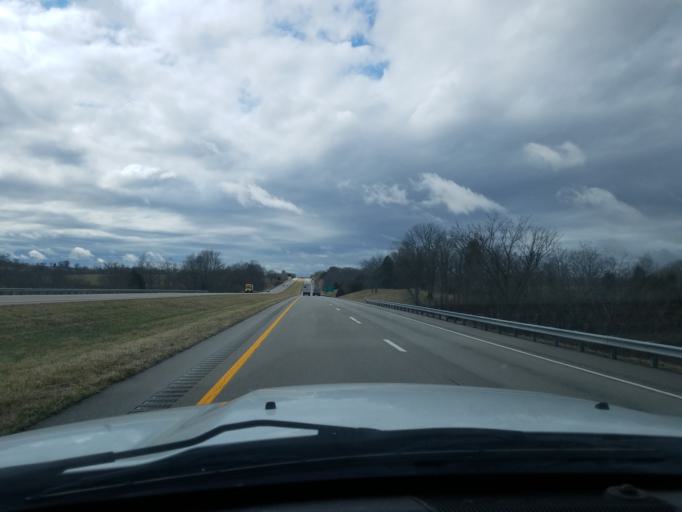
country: US
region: Kentucky
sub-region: Montgomery County
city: Mount Sterling
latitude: 38.0978
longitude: -83.8568
